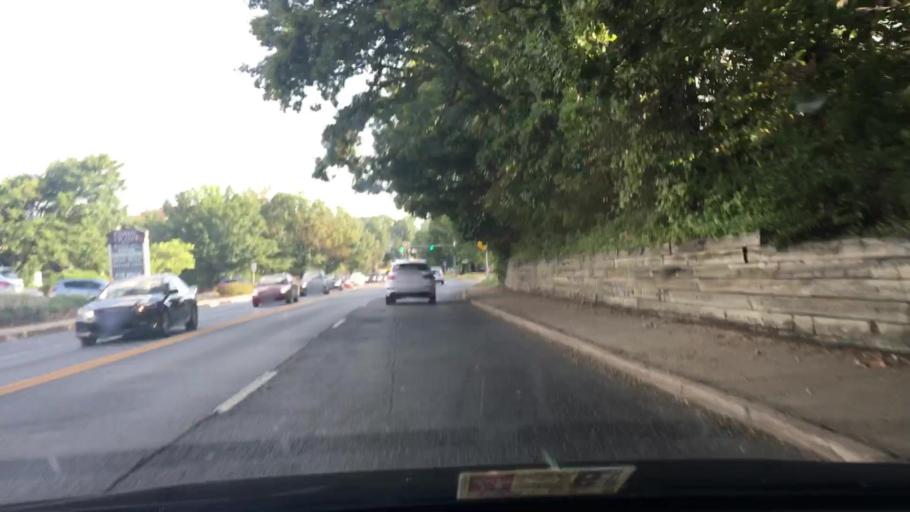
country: US
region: Maryland
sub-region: Montgomery County
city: North Bethesda
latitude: 39.0578
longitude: -77.1264
